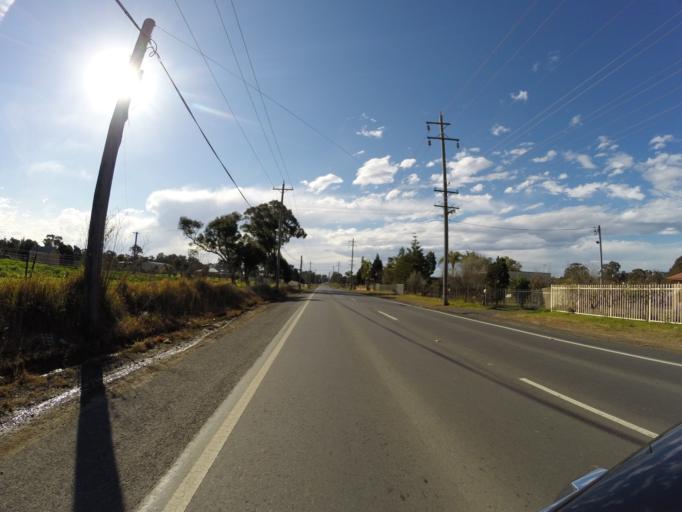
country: AU
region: New South Wales
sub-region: Fairfield
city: Cecil Park
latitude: -33.8870
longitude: 150.7915
